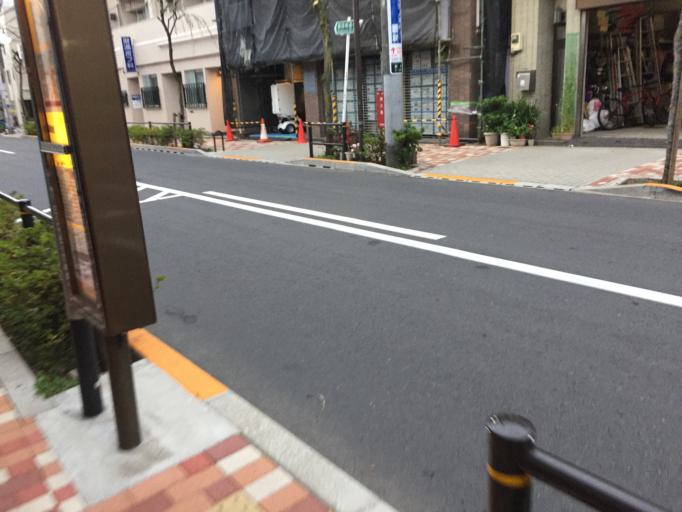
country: JP
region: Tokyo
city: Tokyo
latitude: 35.7124
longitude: 139.6688
